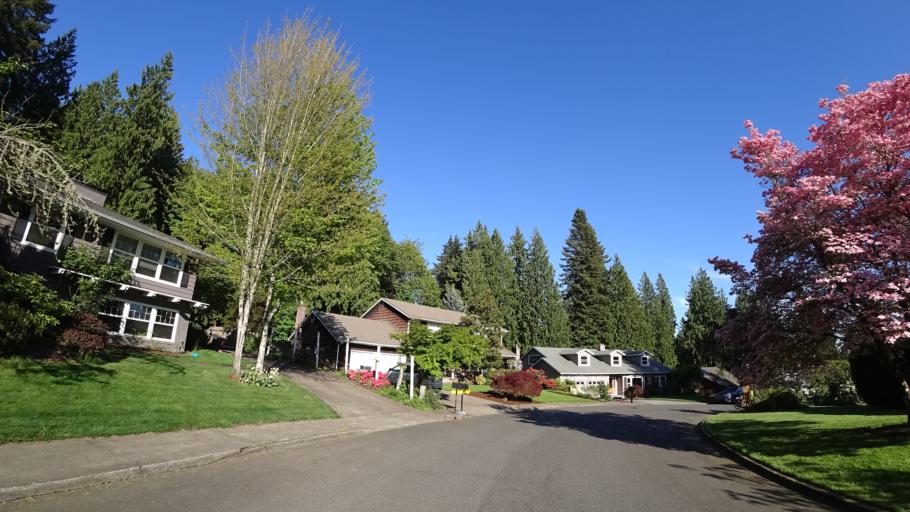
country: US
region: Oregon
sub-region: Washington County
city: West Slope
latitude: 45.4997
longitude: -122.7561
